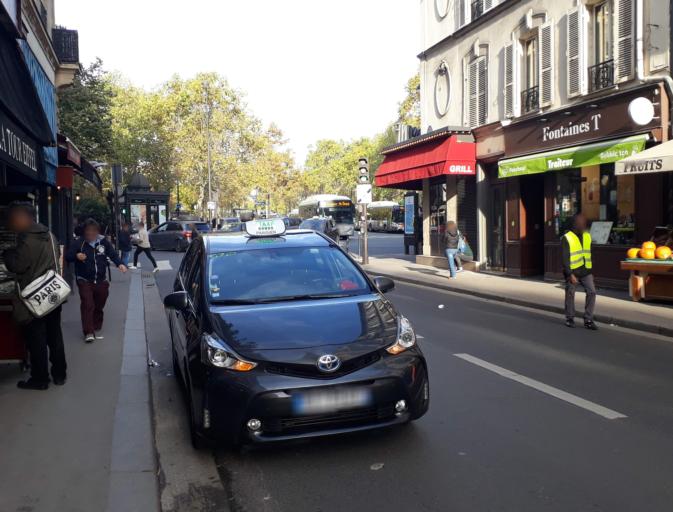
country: FR
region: Ile-de-France
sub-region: Departement des Hauts-de-Seine
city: Vanves
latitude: 48.8544
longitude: 2.2950
